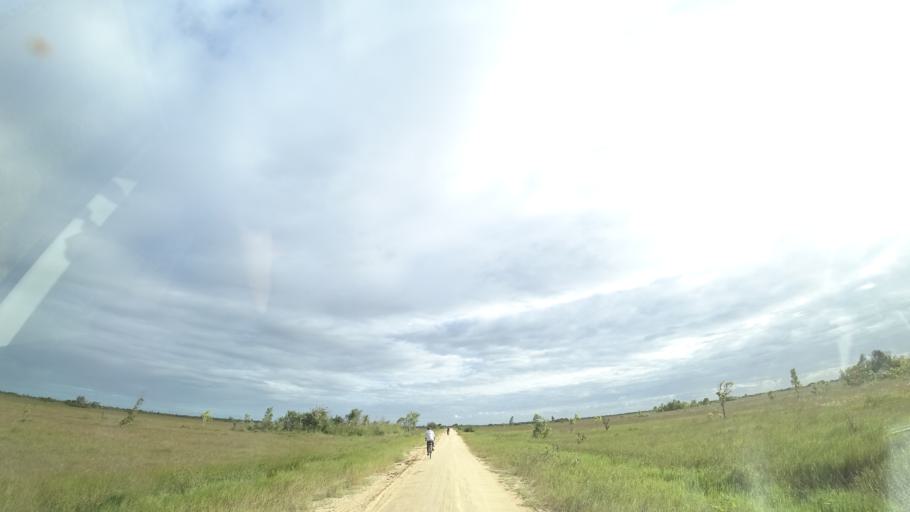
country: MZ
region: Sofala
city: Beira
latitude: -19.6921
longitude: 35.0394
